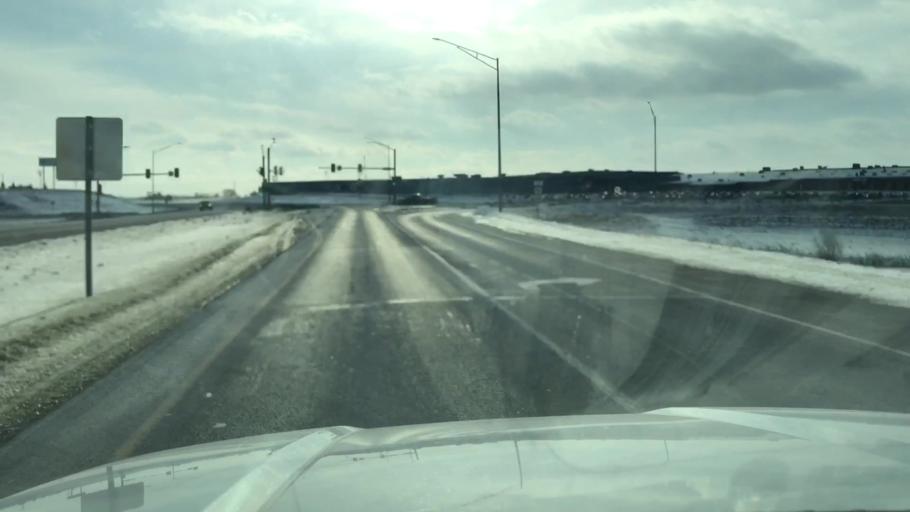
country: US
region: Missouri
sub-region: Nodaway County
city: Maryville
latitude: 40.3148
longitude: -94.8721
